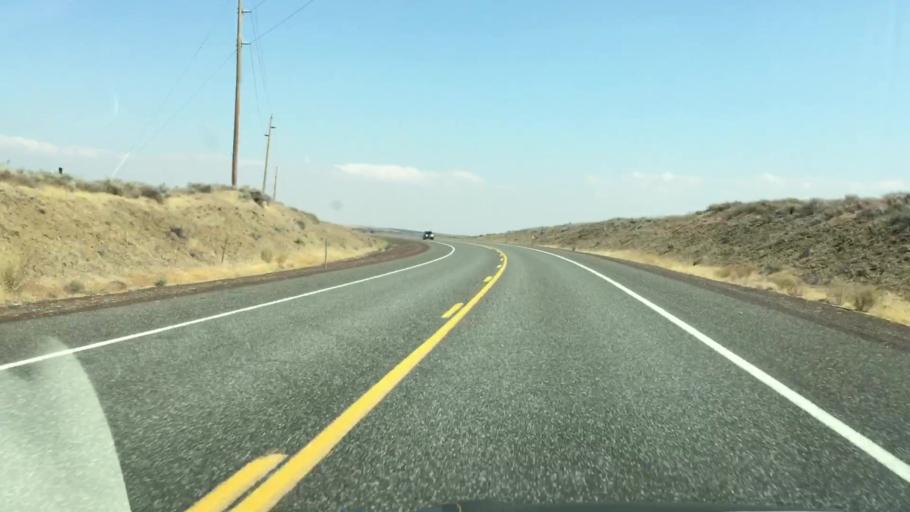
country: US
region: Oregon
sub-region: Wasco County
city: The Dalles
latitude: 45.3358
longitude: -121.1430
